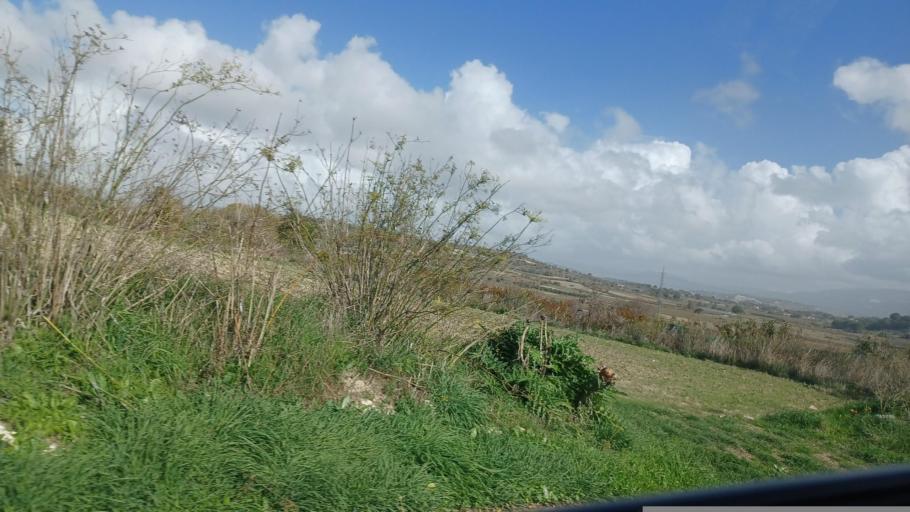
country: CY
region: Pafos
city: Tala
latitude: 34.8877
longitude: 32.4880
